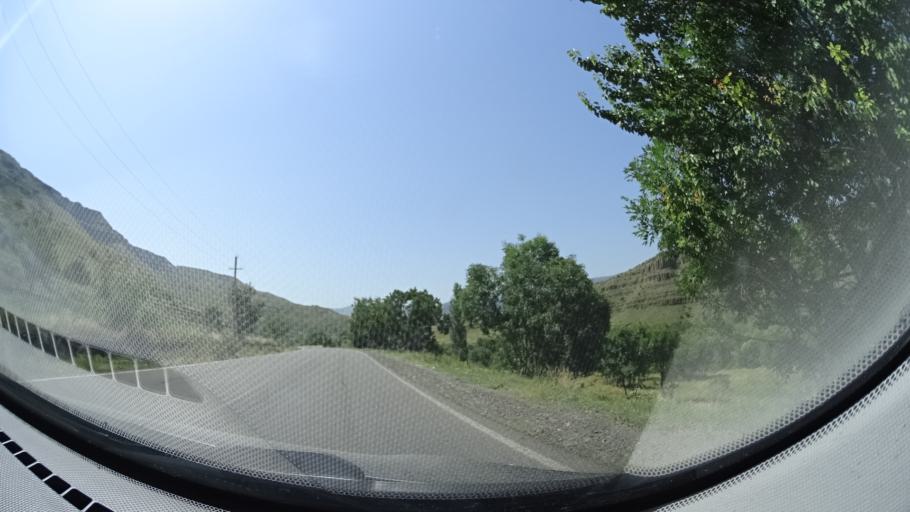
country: GE
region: Samtskhe-Javakheti
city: Aspindza
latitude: 41.5373
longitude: 43.2587
